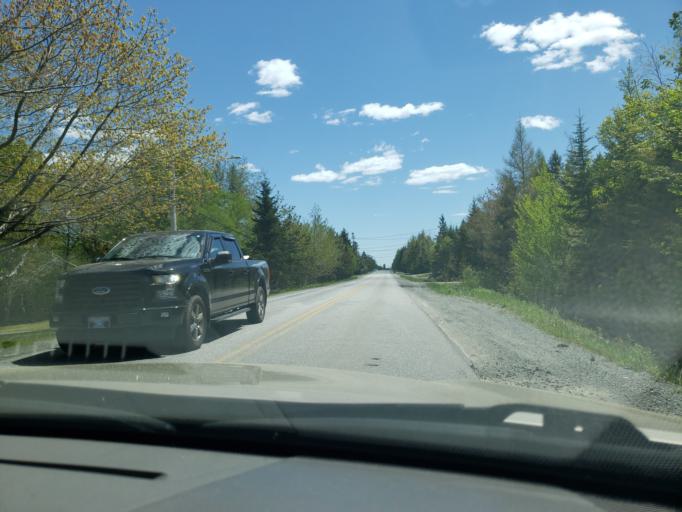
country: CA
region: Nova Scotia
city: Cole Harbour
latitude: 44.7355
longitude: -63.3100
